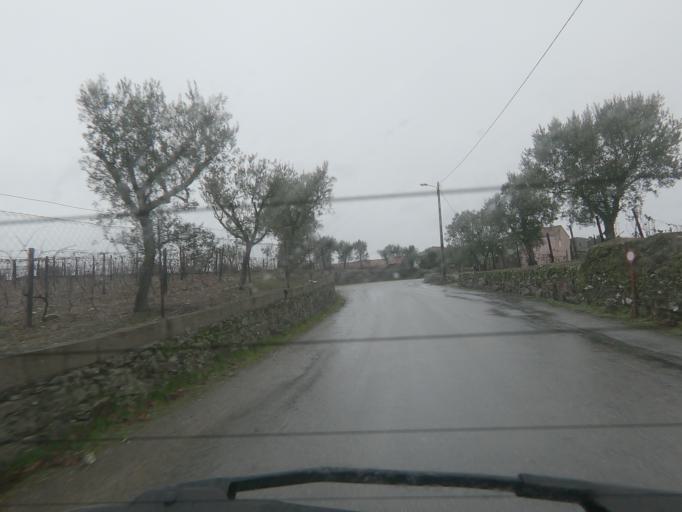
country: PT
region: Vila Real
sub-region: Peso da Regua
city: Peso da Regua
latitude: 41.2002
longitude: -7.7046
